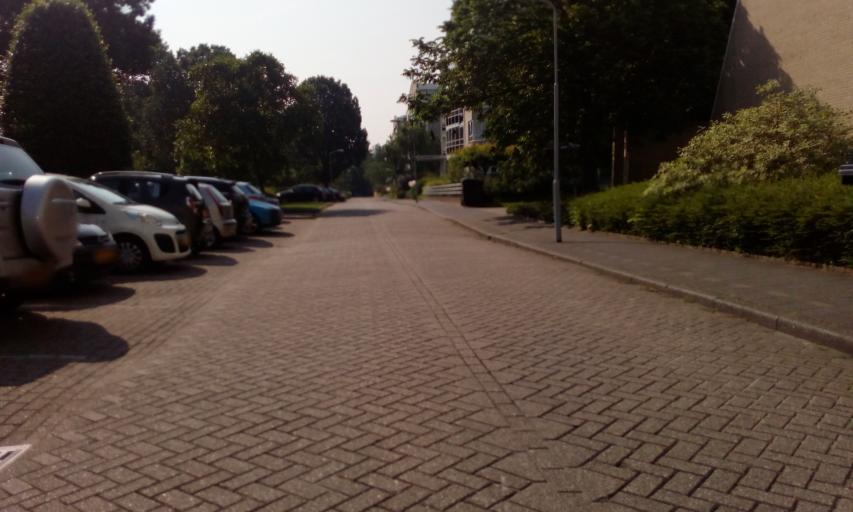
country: NL
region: South Holland
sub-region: Gemeente Leidschendam-Voorburg
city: Voorburg
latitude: 52.0751
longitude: 4.3629
